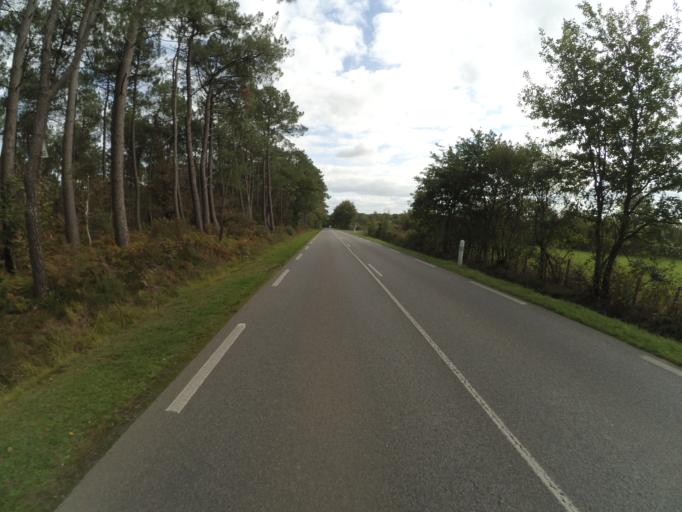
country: FR
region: Pays de la Loire
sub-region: Departement de la Loire-Atlantique
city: Plesse
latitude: 47.4885
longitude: -1.8559
